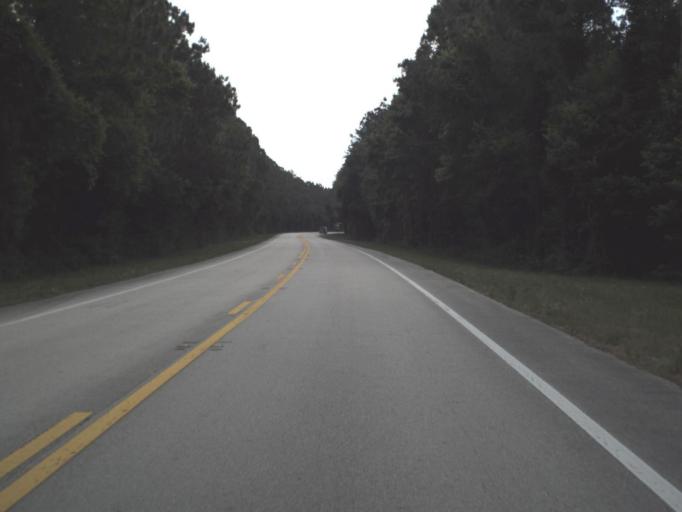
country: US
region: Florida
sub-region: Saint Johns County
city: Saint Augustine Shores
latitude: 29.7262
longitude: -81.4212
